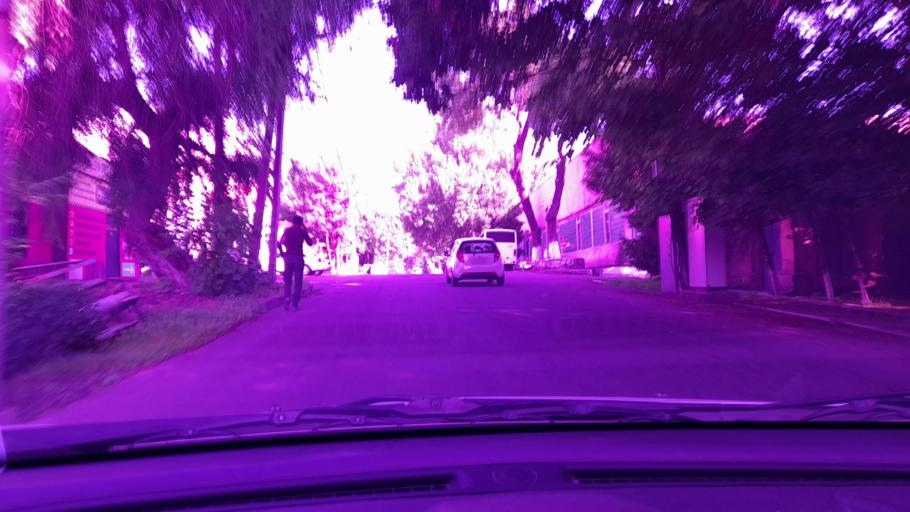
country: UZ
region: Toshkent
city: Salor
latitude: 41.3351
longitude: 69.3560
